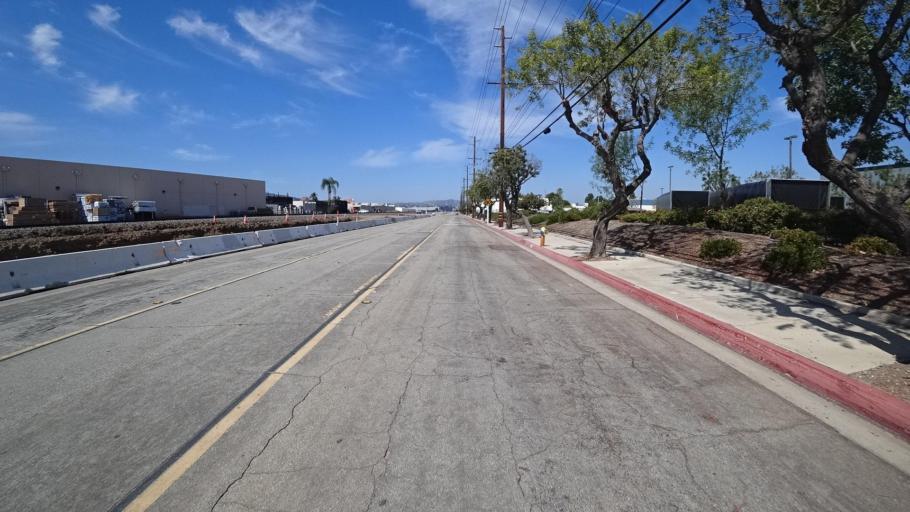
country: US
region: California
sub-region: Los Angeles County
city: South San Jose Hills
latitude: 33.9970
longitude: -117.9074
